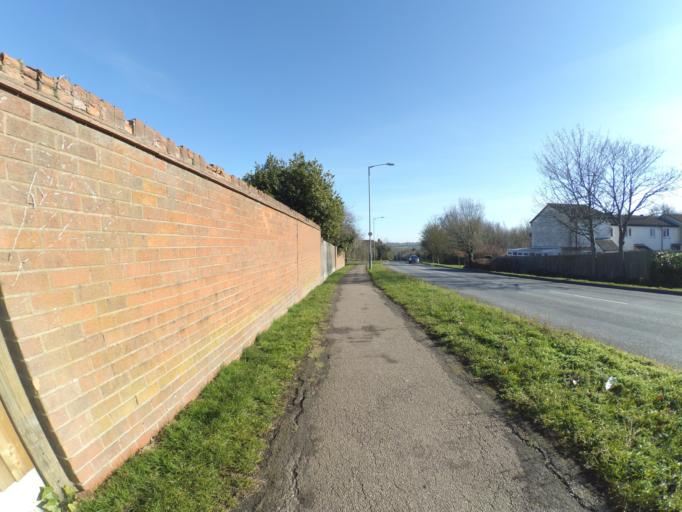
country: GB
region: England
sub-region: Warwickshire
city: Rugby
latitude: 52.3934
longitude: -1.2395
